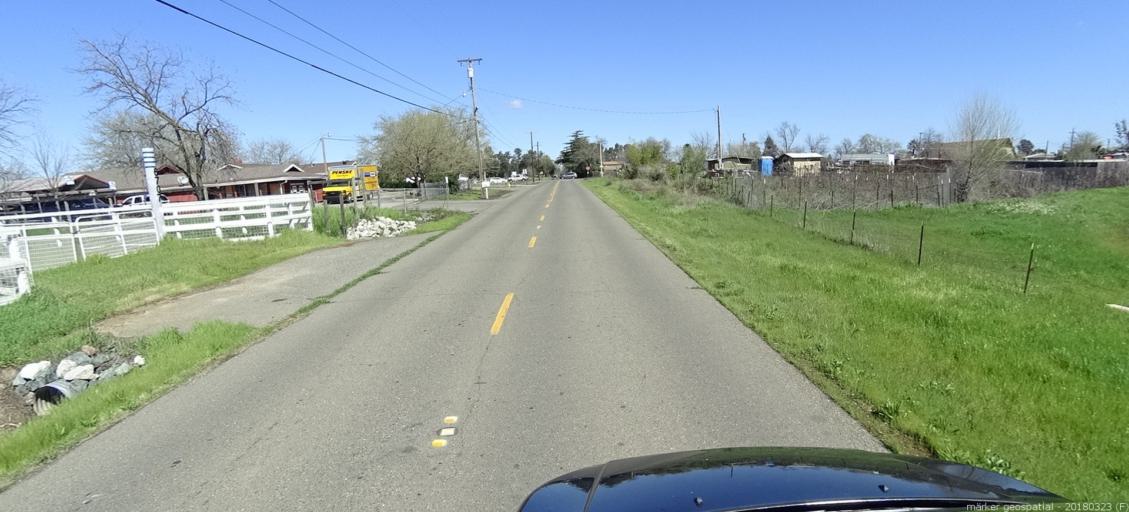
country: US
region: California
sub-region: Sacramento County
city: Rio Linda
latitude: 38.6893
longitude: -121.4198
